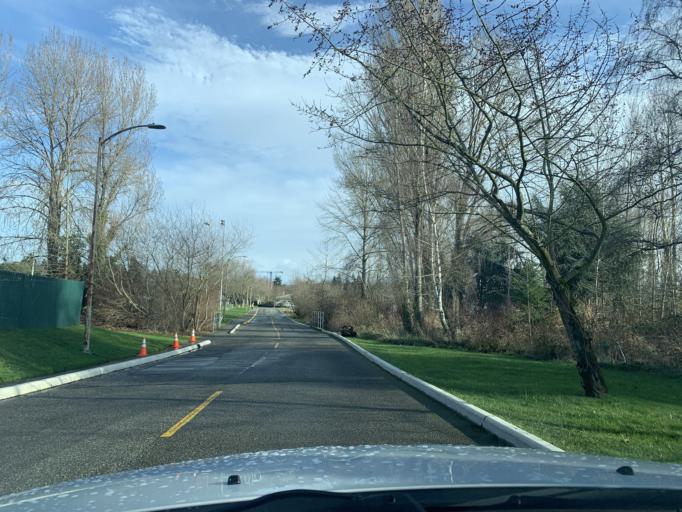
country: US
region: Washington
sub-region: King County
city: Seattle
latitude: 47.6587
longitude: -122.2965
